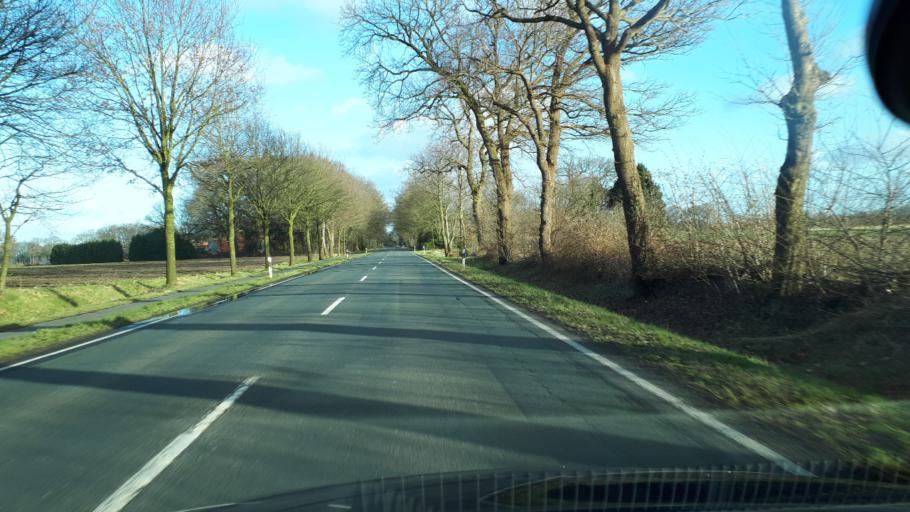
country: DE
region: Lower Saxony
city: Molbergen
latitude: 52.8783
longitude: 7.8734
